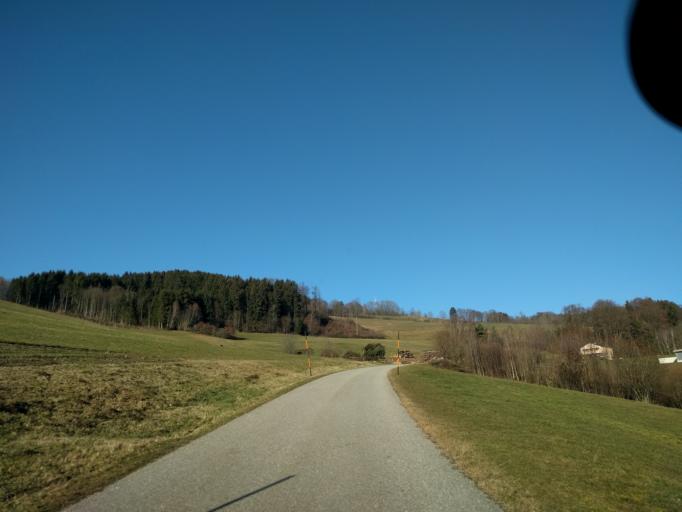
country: AT
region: Upper Austria
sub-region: Politischer Bezirk Urfahr-Umgebung
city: Kirchschlag bei Linz
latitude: 48.4001
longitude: 14.2891
